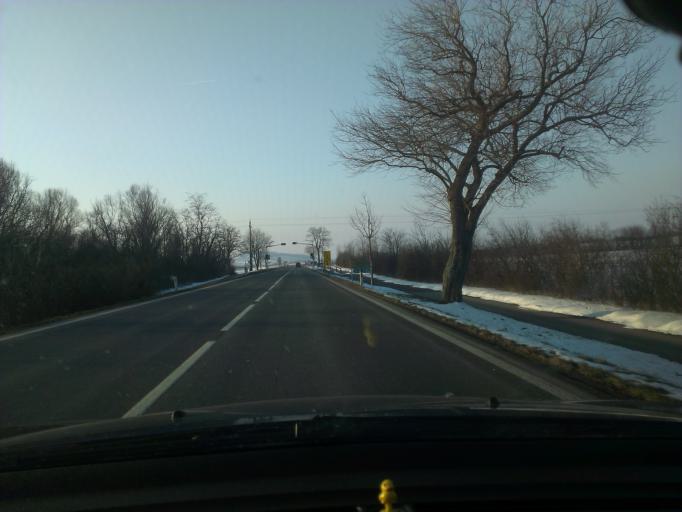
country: AT
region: Burgenland
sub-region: Eisenstadt-Umgebung
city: Donnerskirchen
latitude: 47.8718
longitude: 16.6483
